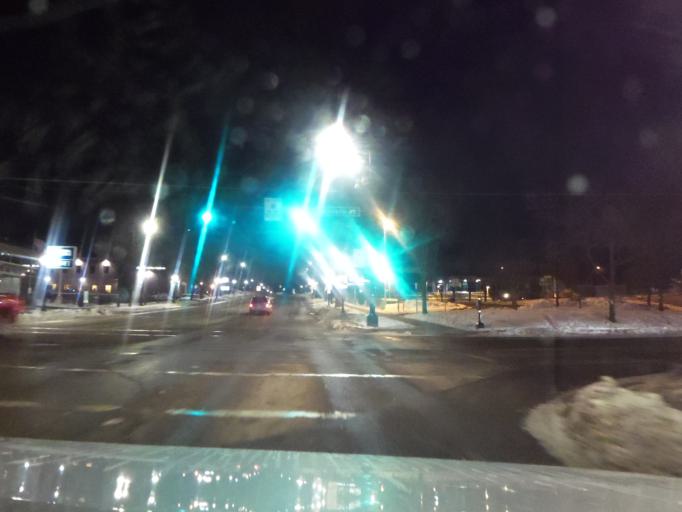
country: US
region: Minnesota
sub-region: Dakota County
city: Mendota Heights
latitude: 44.9179
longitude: -93.1850
